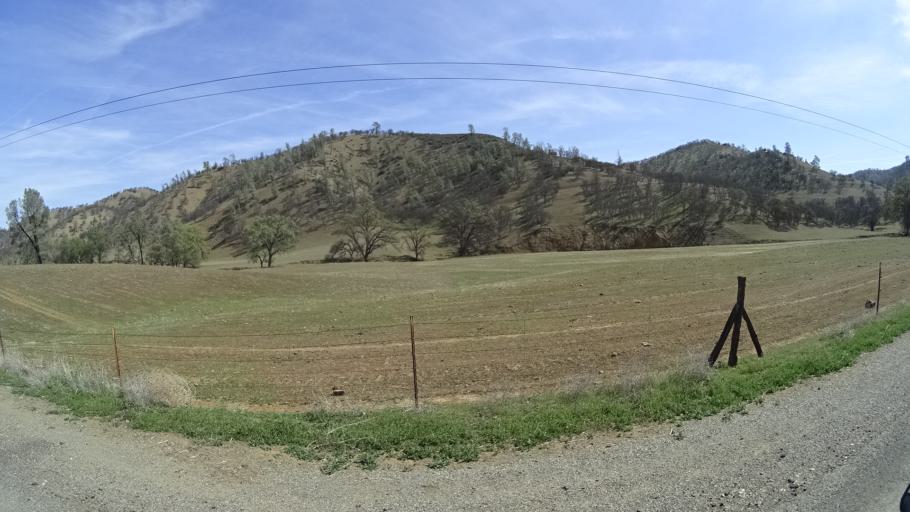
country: US
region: California
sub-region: Glenn County
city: Willows
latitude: 39.4774
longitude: -122.4516
